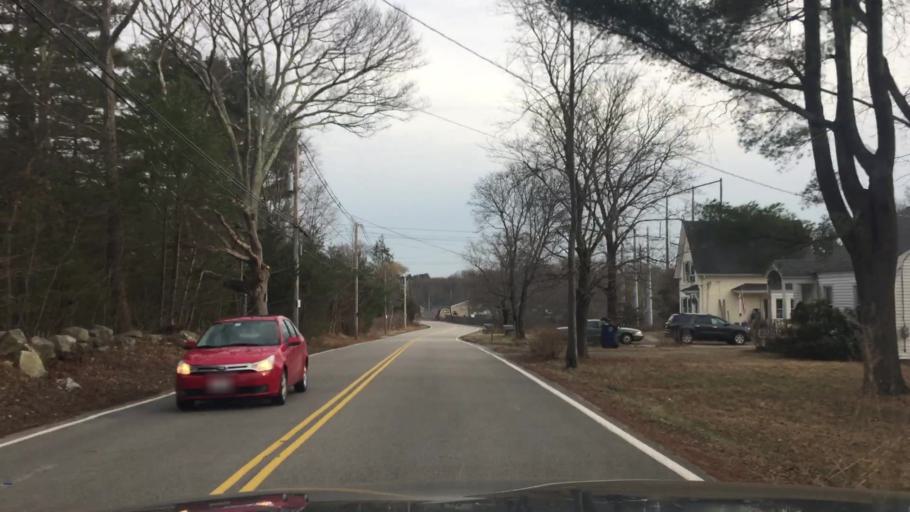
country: US
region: Massachusetts
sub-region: Norfolk County
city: Medway
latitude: 42.1388
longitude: -71.4507
